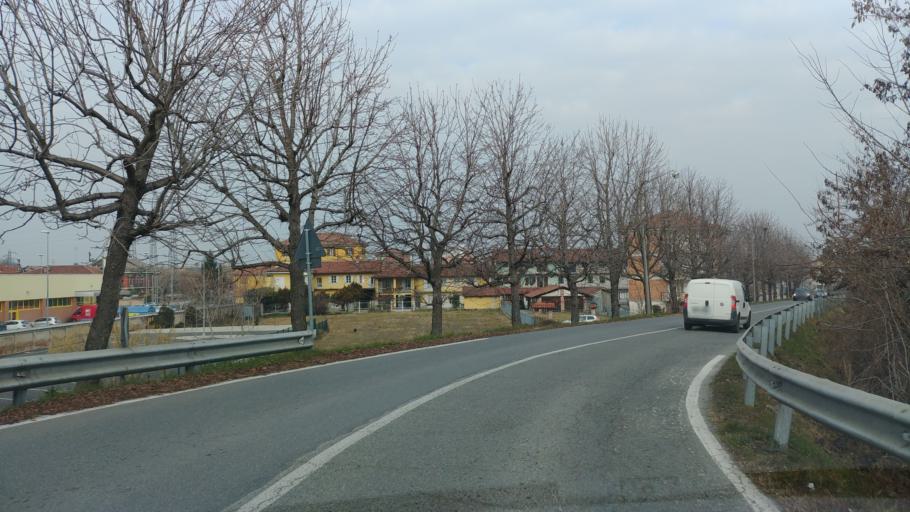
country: IT
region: Piedmont
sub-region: Provincia di Cuneo
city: Fossano
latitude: 44.5456
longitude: 7.7158
